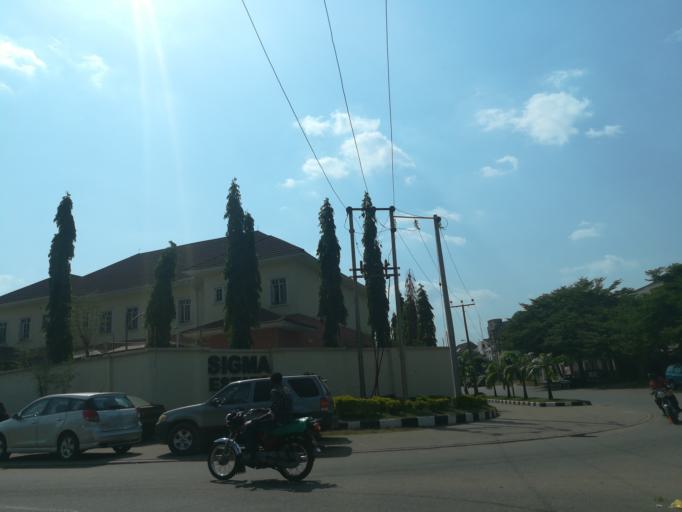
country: NG
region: Abuja Federal Capital Territory
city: Abuja
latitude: 9.0642
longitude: 7.4303
